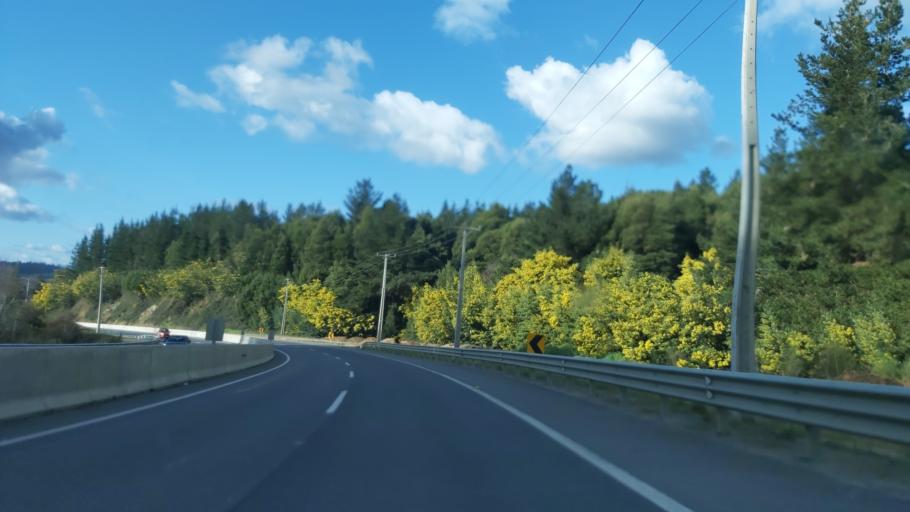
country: CL
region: Biobio
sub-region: Provincia de Concepcion
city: Chiguayante
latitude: -36.8528
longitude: -72.9092
